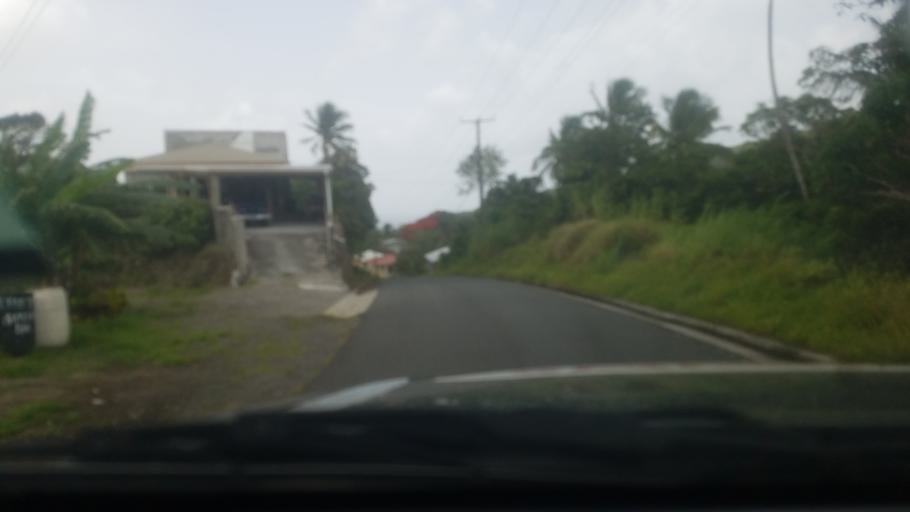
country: LC
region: Laborie Quarter
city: Laborie
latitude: 13.7741
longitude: -60.9928
